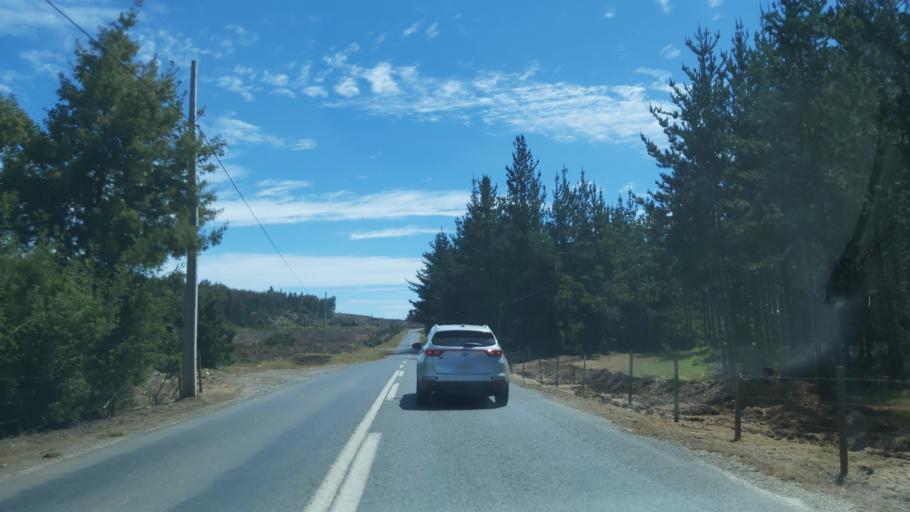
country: CL
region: Maule
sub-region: Provincia de Talca
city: Constitucion
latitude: -35.5379
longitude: -72.5483
